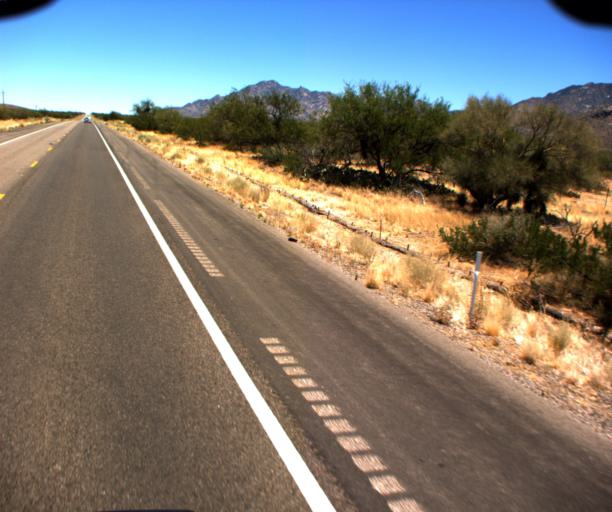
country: US
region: Arizona
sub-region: Pima County
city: Sells
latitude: 32.0100
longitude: -111.6631
